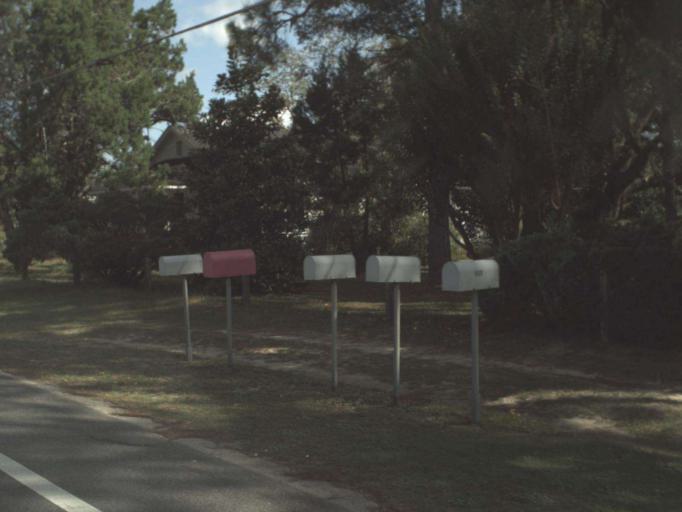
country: US
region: Florida
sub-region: Walton County
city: DeFuniak Springs
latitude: 30.7280
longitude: -86.1147
